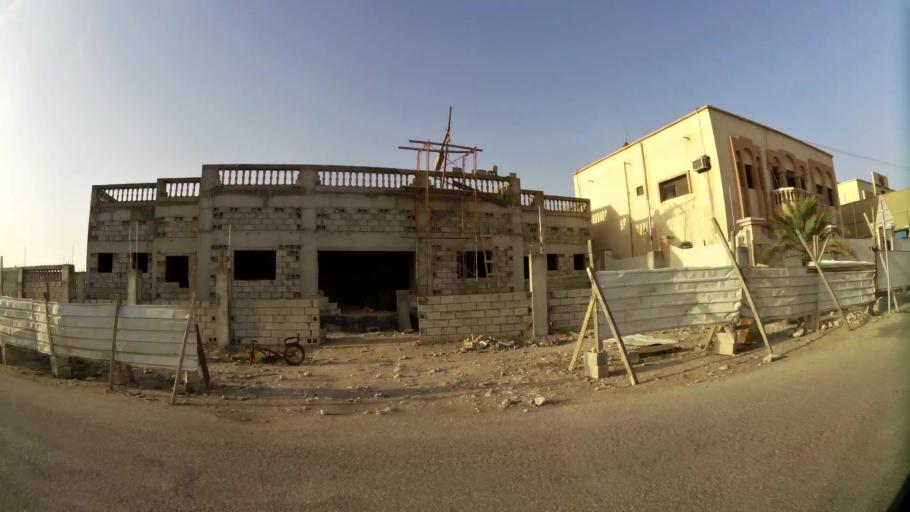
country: QA
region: Baladiyat ar Rayyan
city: Ar Rayyan
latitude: 25.3231
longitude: 51.4564
